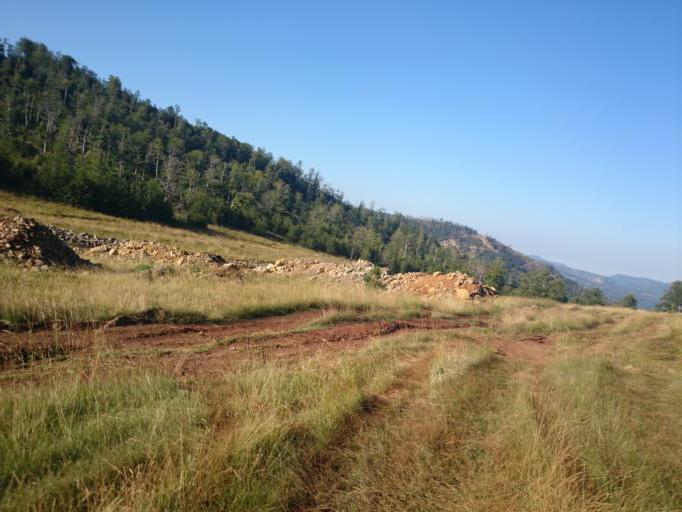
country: AL
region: Diber
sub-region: Rrethi i Bulqizes
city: Martanesh
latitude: 41.4061
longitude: 20.3088
